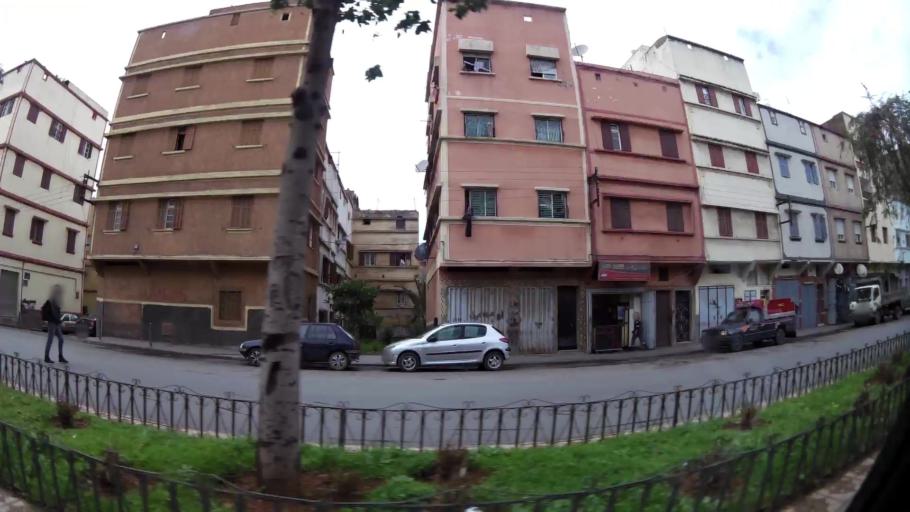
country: MA
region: Grand Casablanca
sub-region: Casablanca
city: Casablanca
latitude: 33.5453
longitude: -7.5661
